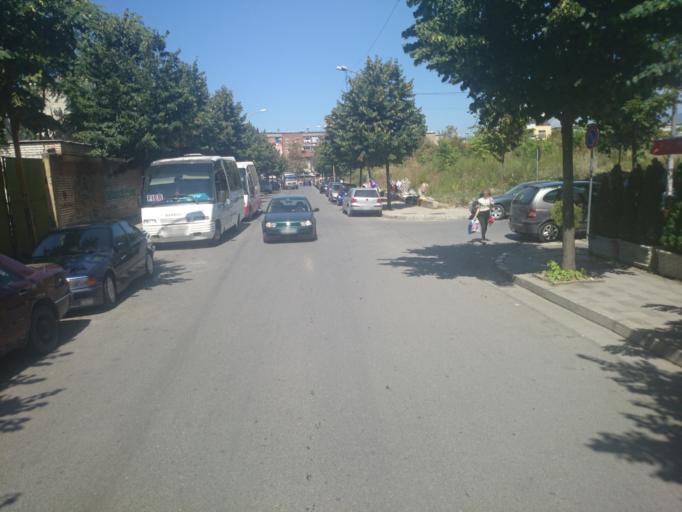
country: AL
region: Tirane
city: Tirana
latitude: 41.3228
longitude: 19.7980
